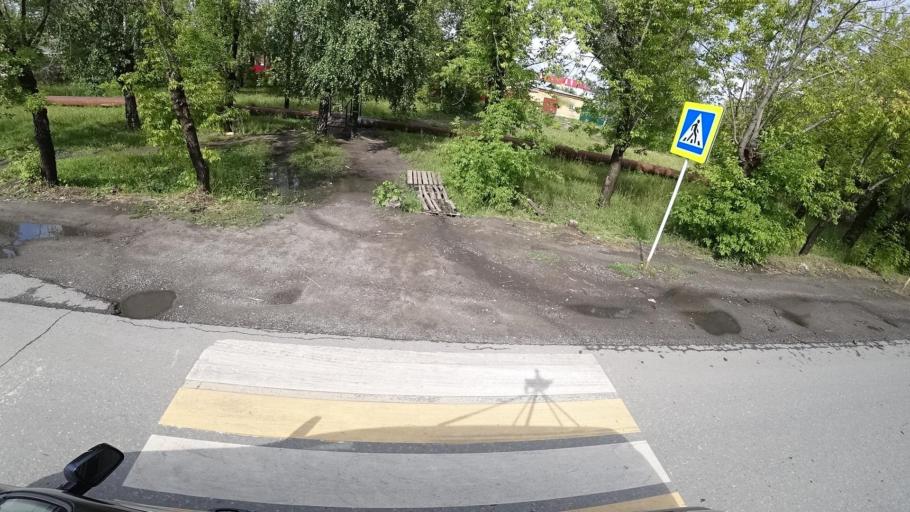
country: RU
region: Sverdlovsk
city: Kamyshlov
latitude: 56.8440
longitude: 62.7190
